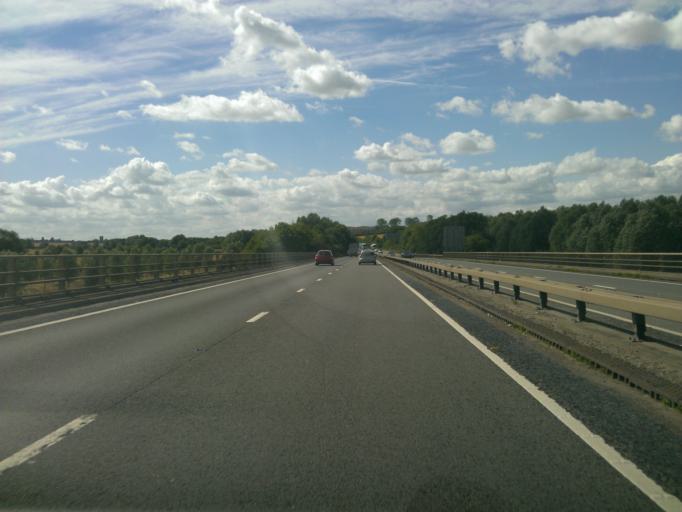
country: GB
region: England
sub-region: Northamptonshire
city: Thrapston
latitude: 52.3898
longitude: -0.5417
